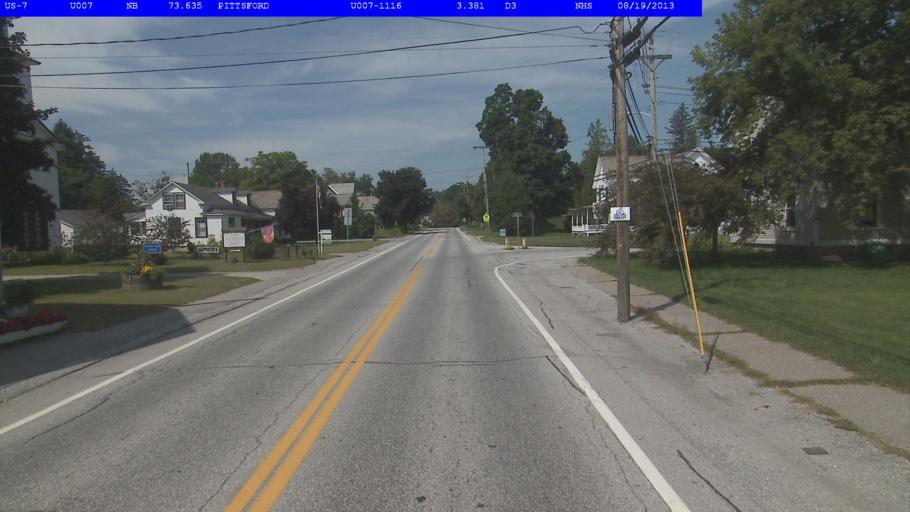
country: US
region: Vermont
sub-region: Rutland County
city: Rutland
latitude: 43.7065
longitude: -73.0164
